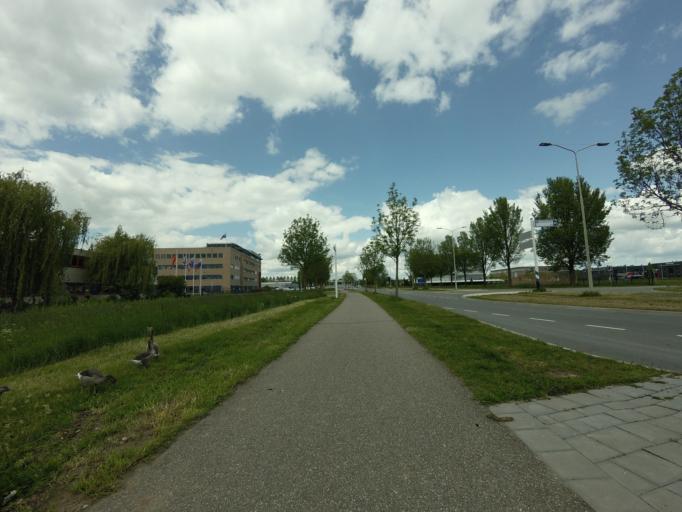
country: NL
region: North Brabant
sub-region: Gemeente Woudrichem
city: Woudrichem
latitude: 51.8383
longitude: 5.0043
